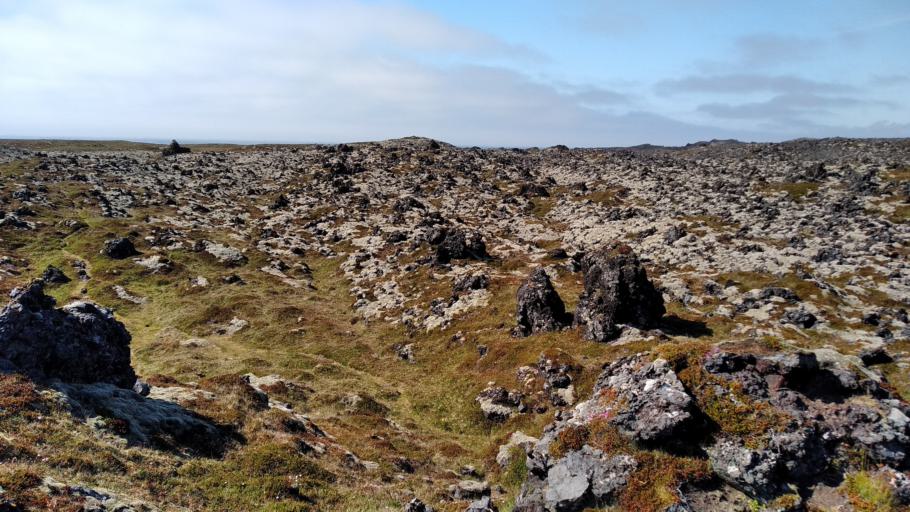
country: IS
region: West
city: Olafsvik
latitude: 64.7522
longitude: -23.9084
